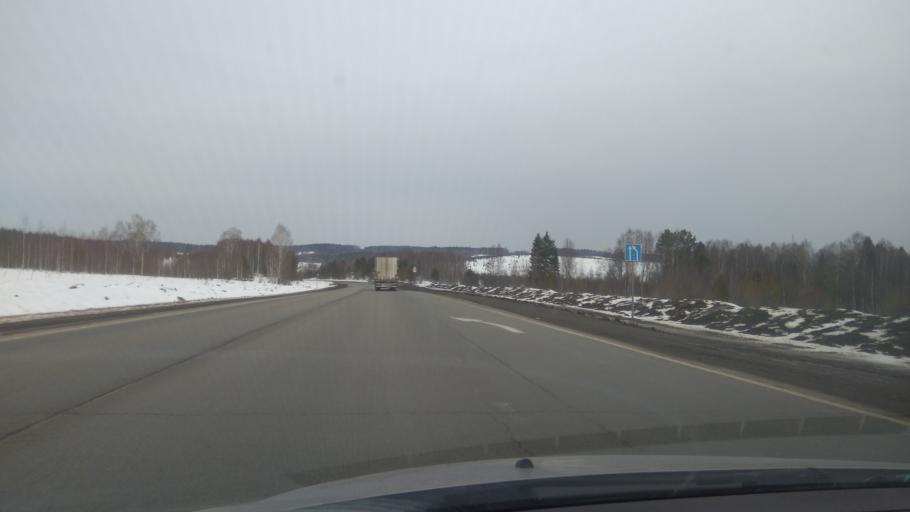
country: RU
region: Sverdlovsk
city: Ufimskiy
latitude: 56.7882
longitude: 58.3577
